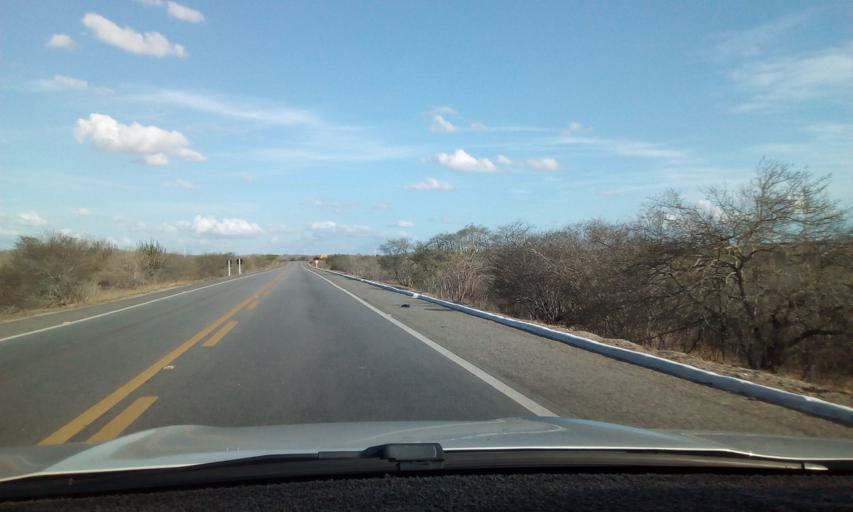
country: BR
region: Paraiba
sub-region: Pocinhos
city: Pocinhos
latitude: -7.1448
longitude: -36.1333
